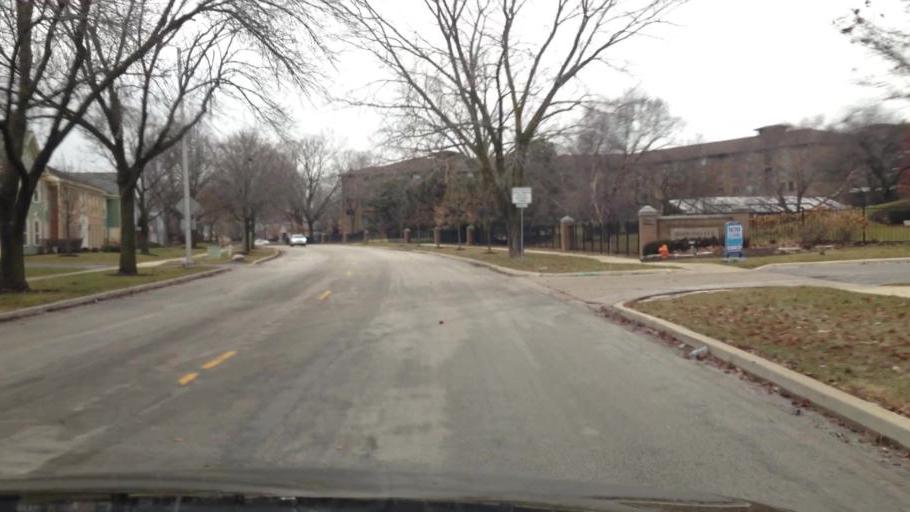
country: US
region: Illinois
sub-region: DuPage County
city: Naperville
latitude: 41.7974
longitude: -88.1281
